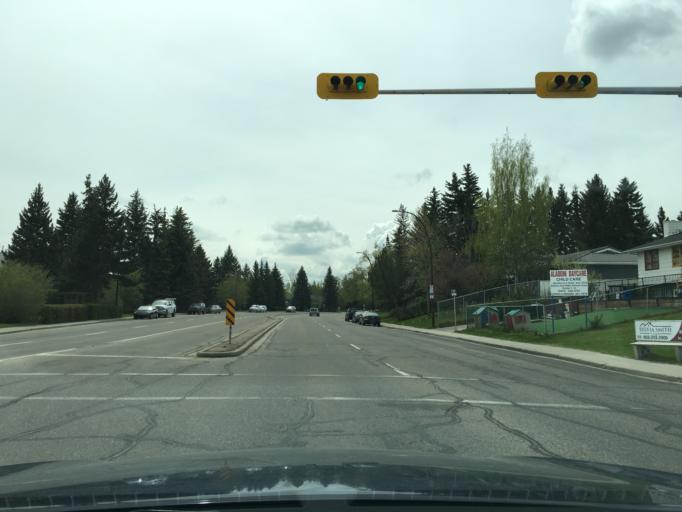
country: CA
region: Alberta
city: Calgary
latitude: 50.9478
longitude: -114.0846
